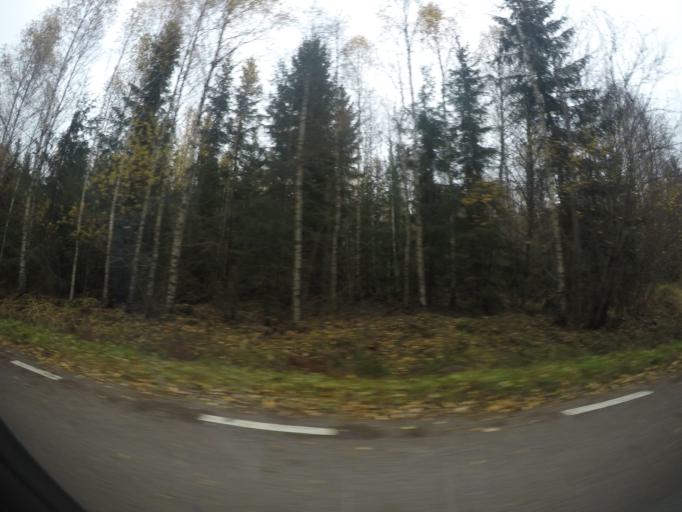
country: SE
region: Vaestmanland
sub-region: Surahammars Kommun
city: Surahammar
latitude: 59.6718
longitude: 16.0768
